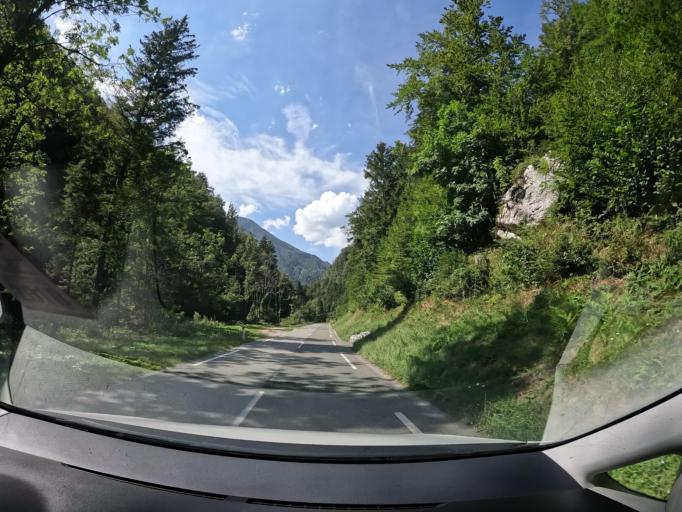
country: SI
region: Jezersko
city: Zgornje Jezersko
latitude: 46.3570
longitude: 14.4652
